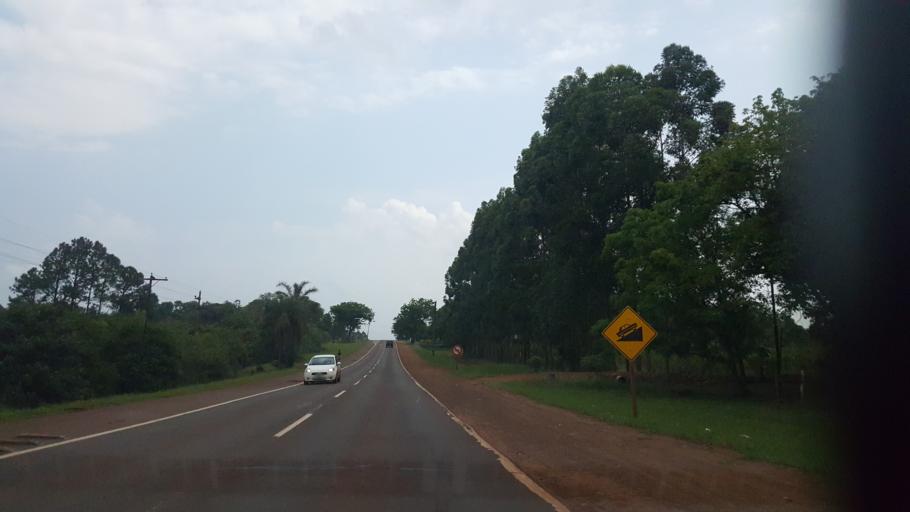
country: AR
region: Misiones
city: Jardin America
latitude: -27.0654
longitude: -55.2655
